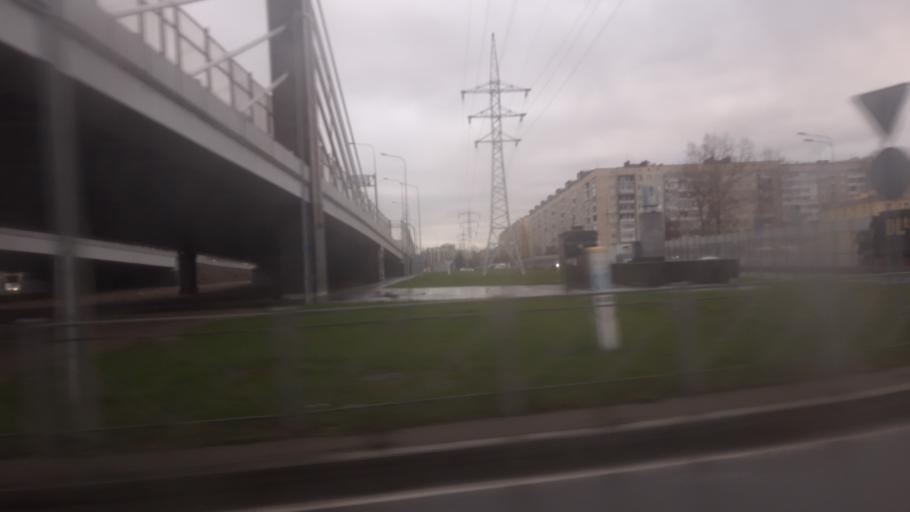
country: RU
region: St.-Petersburg
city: Kupchino
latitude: 59.8301
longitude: 30.3230
